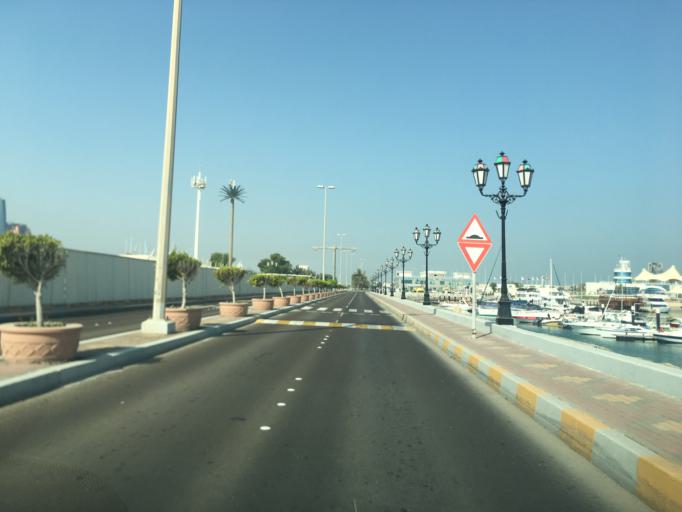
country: AE
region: Abu Dhabi
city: Abu Dhabi
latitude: 24.4750
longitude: 54.3278
